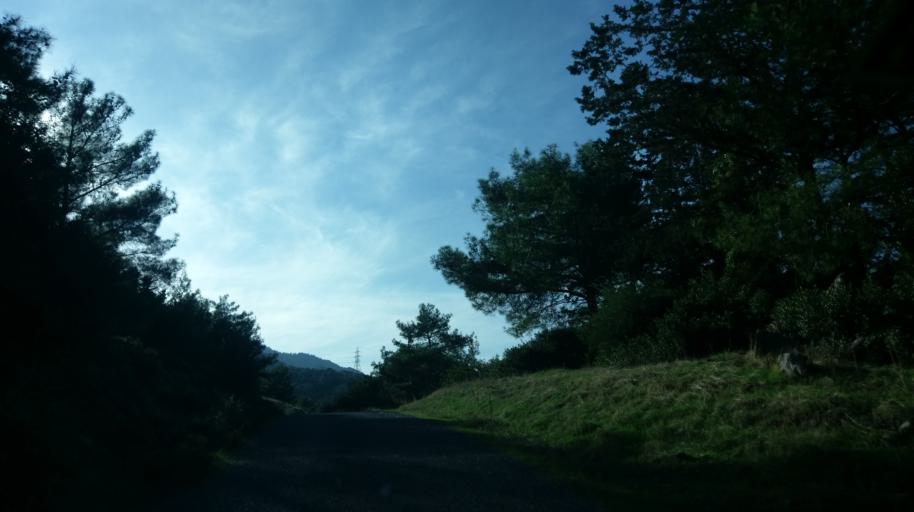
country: CY
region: Ammochostos
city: Lefkonoiko
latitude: 35.3257
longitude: 33.6289
